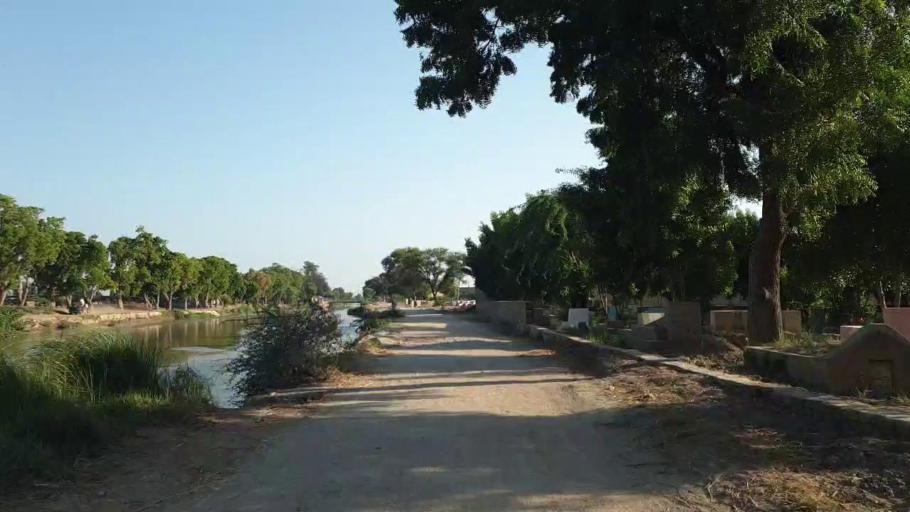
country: PK
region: Sindh
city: Hyderabad
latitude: 25.3189
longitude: 68.4285
